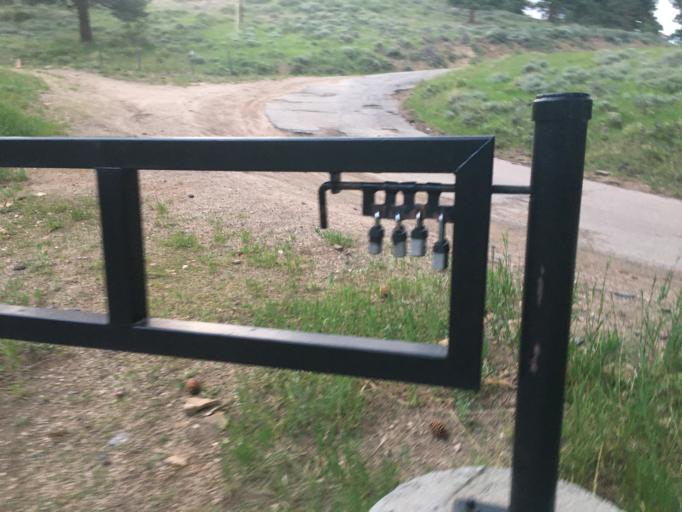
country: US
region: Colorado
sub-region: Larimer County
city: Estes Park
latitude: 40.3363
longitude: -105.5826
